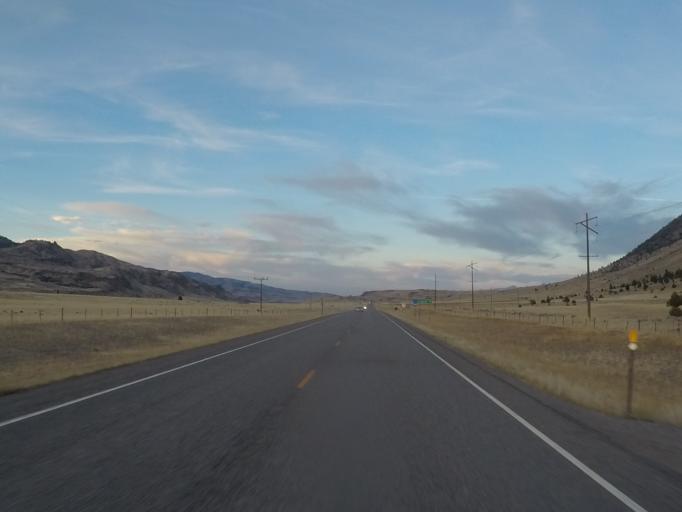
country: US
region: Montana
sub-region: Gallatin County
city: Big Sky
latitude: 45.2075
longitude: -110.8935
